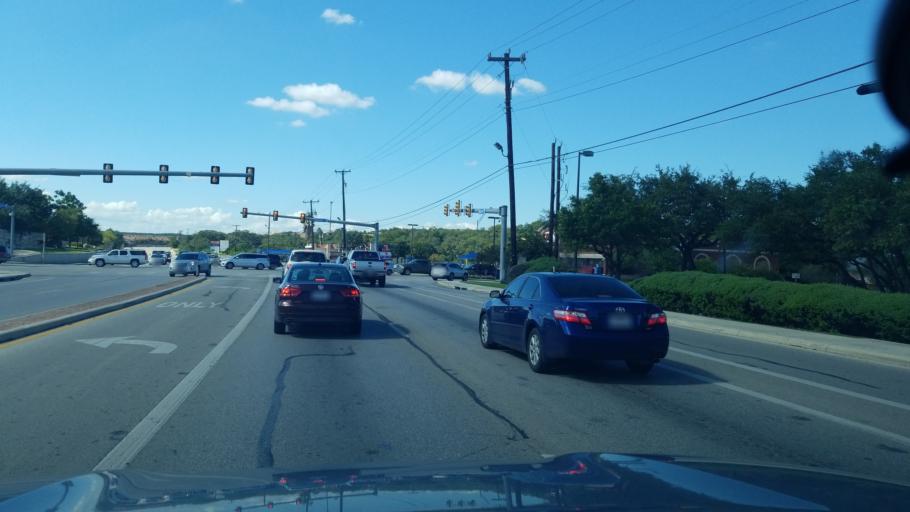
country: US
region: Texas
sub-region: Bexar County
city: Hollywood Park
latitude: 29.6208
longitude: -98.5126
